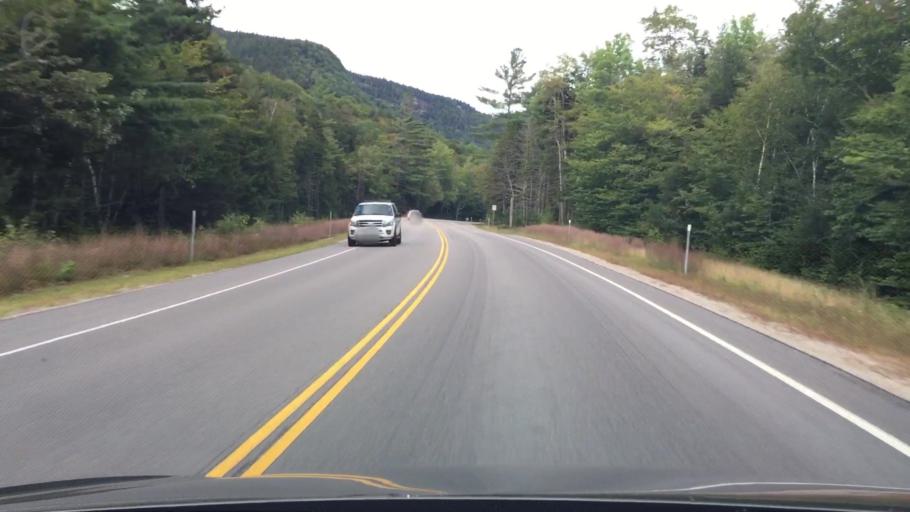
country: US
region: New Hampshire
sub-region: Carroll County
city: North Conway
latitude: 44.0094
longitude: -71.2694
